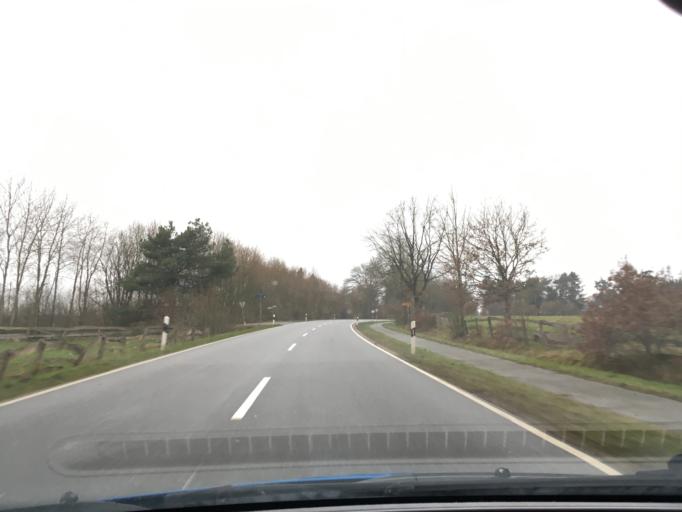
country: DE
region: Schleswig-Holstein
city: Hornbek
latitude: 53.5634
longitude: 10.6458
